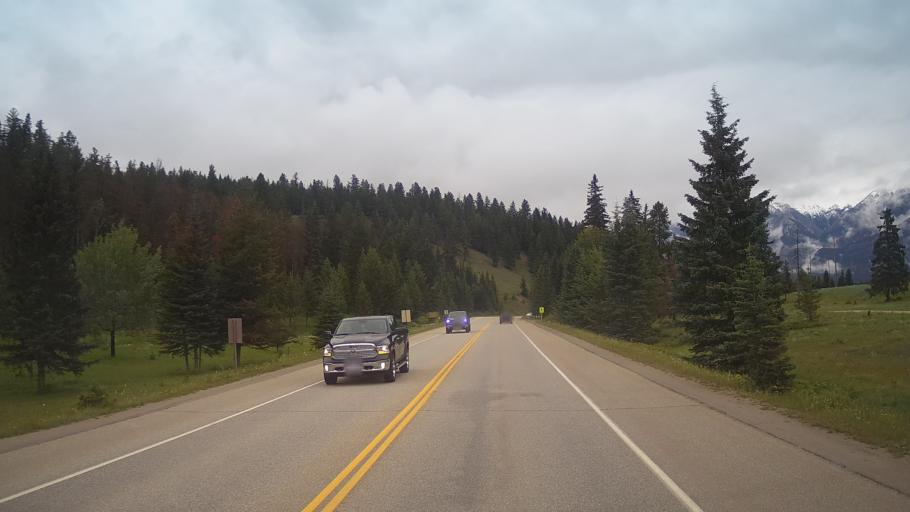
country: CA
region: Alberta
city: Jasper Park Lodge
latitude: 52.8911
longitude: -118.0761
